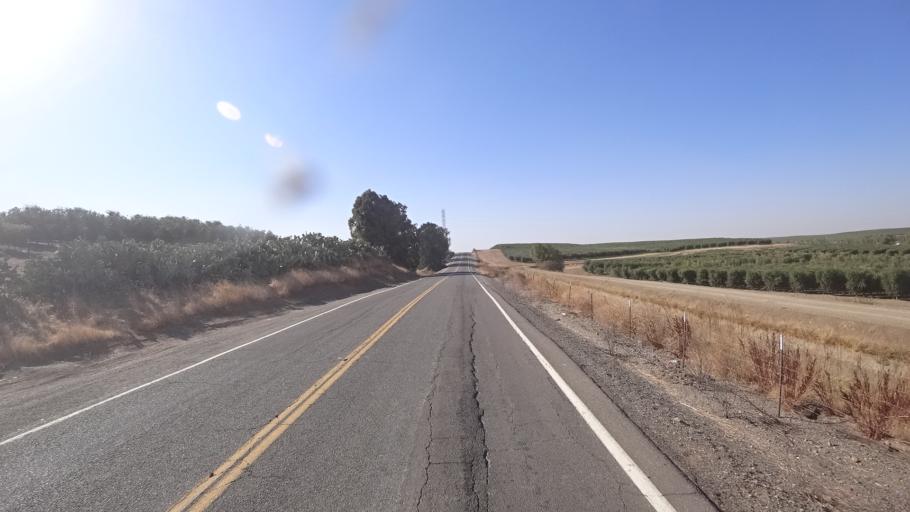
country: US
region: California
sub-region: Yolo County
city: Cottonwood
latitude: 38.7100
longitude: -121.8911
